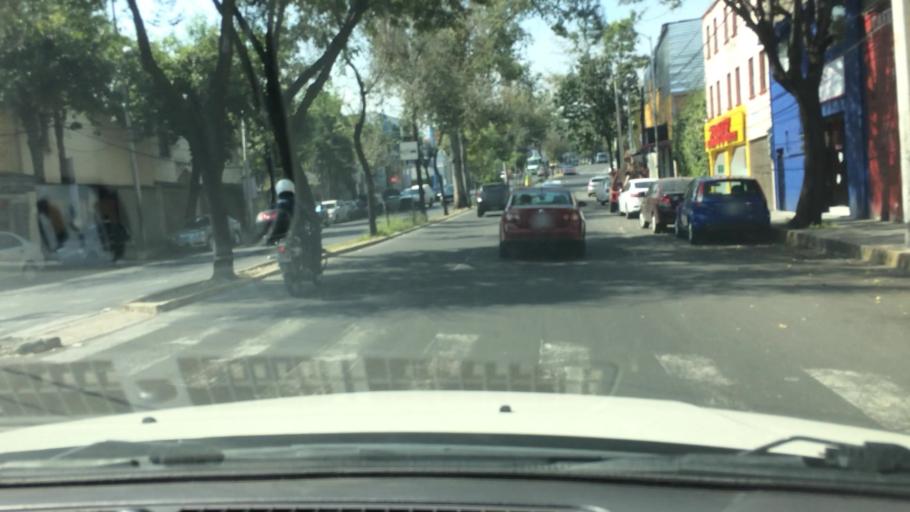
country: MX
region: Mexico City
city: Tlalpan
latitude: 19.2951
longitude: -99.1762
